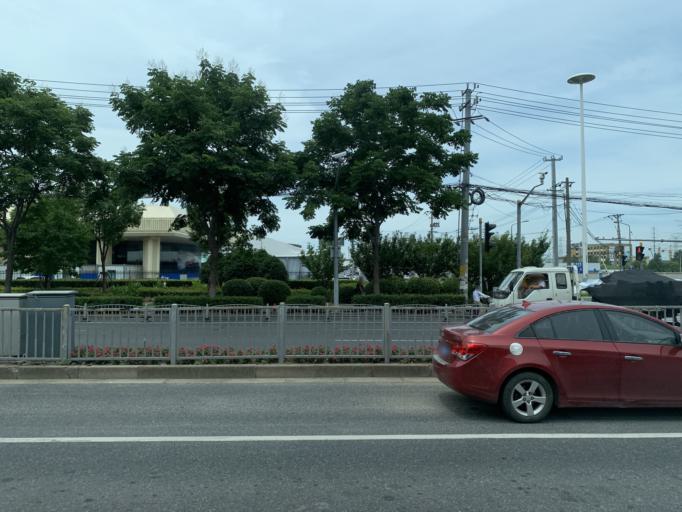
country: CN
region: Shanghai Shi
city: Kangqiao
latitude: 31.1586
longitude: 121.5600
